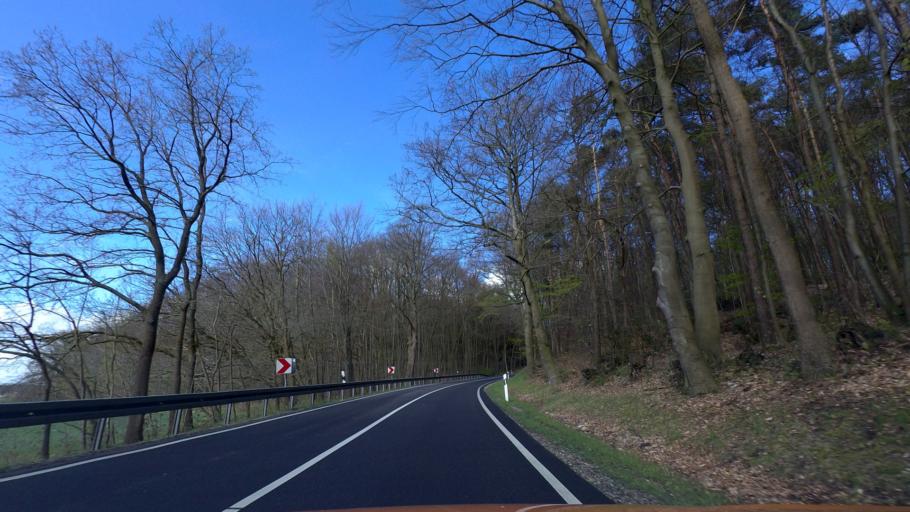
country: DE
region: Schleswig-Holstein
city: Langenlehsten
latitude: 53.4689
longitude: 10.7865
